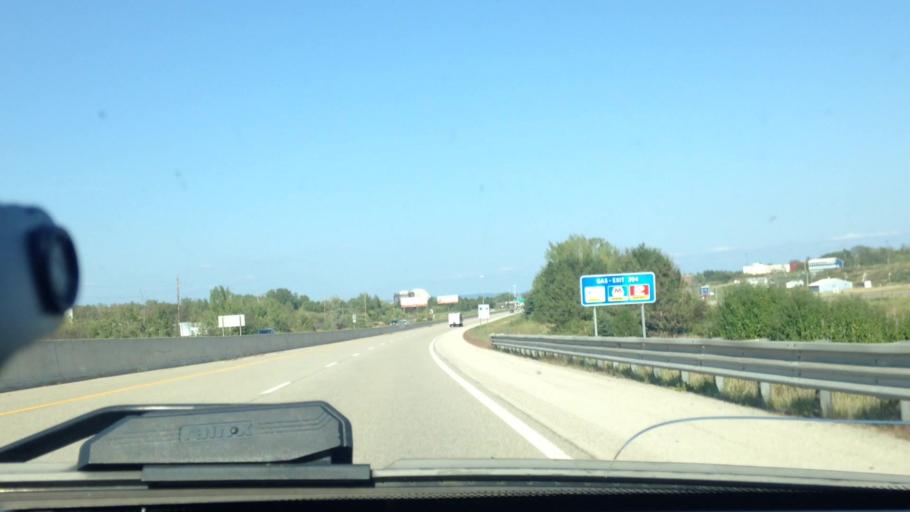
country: US
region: Michigan
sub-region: Chippewa County
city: Sault Ste. Marie
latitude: 46.4842
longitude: -84.3805
